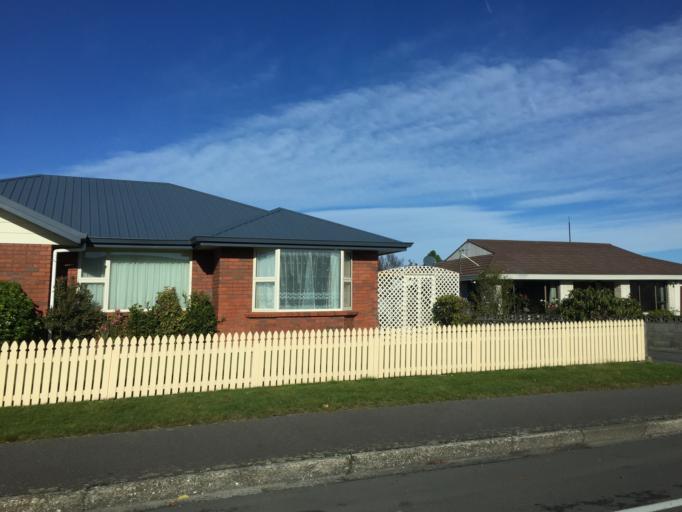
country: NZ
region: Southland
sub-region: Invercargill City
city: Invercargill
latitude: -46.4021
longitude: 168.3693
